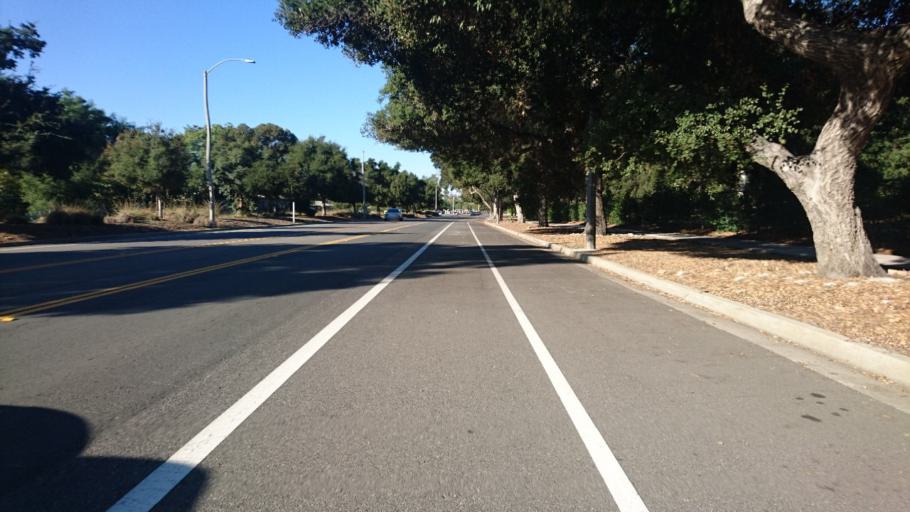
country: US
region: California
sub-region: Los Angeles County
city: Claremont
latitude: 34.0950
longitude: -117.7080
